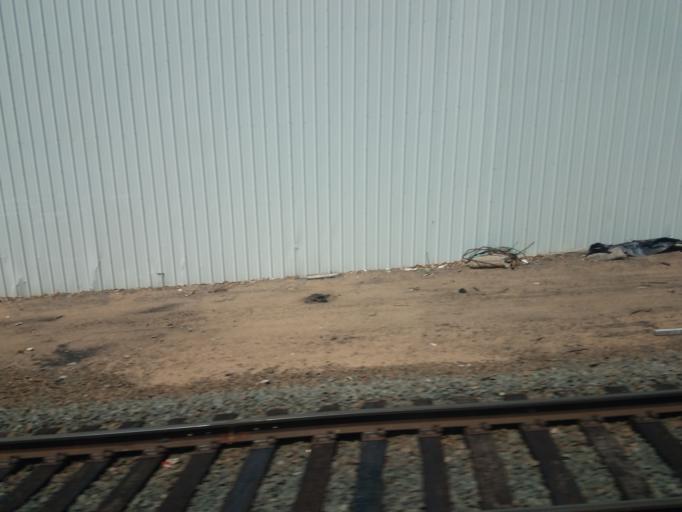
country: US
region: Connecticut
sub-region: New Haven County
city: Wallingford
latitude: 41.4797
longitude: -72.8126
